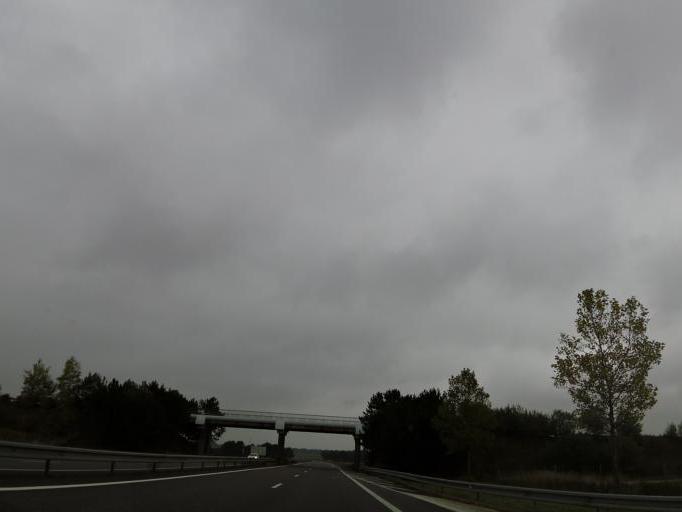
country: FR
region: Champagne-Ardenne
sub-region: Departement de la Marne
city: Courtisols
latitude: 49.0283
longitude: 4.4961
